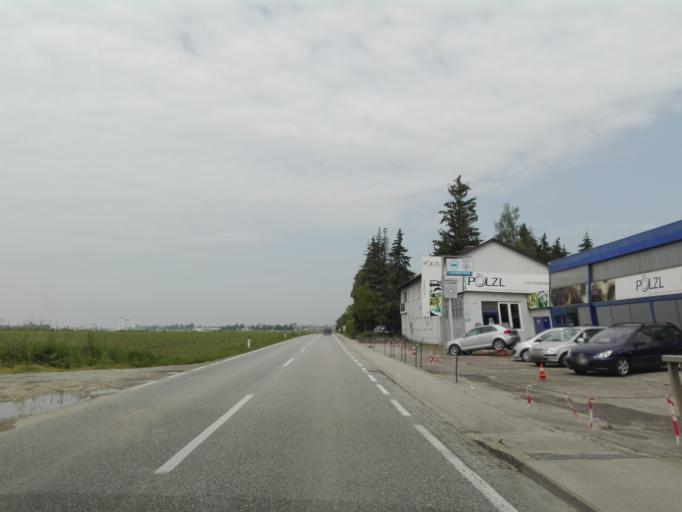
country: AT
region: Upper Austria
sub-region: Politischer Bezirk Urfahr-Umgebung
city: Ottensheim
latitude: 48.2870
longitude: 14.1418
